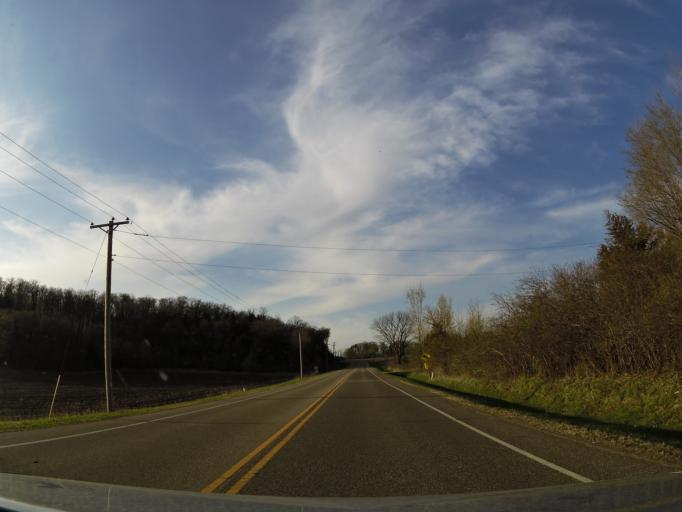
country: US
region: Wisconsin
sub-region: Pierce County
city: River Falls
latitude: 44.8899
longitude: -92.6687
